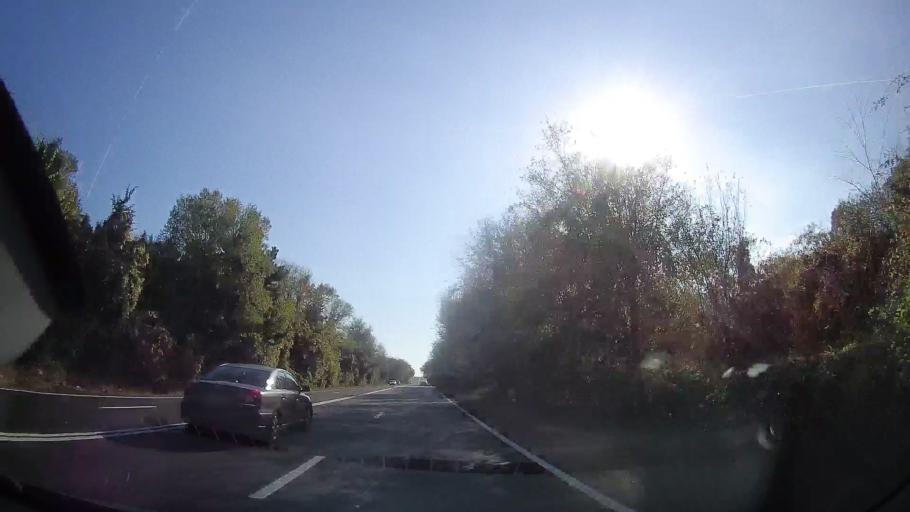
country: RO
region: Constanta
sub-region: Comuna Douazeci si Trei August
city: Dulcesti
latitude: 43.8647
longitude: 28.5751
